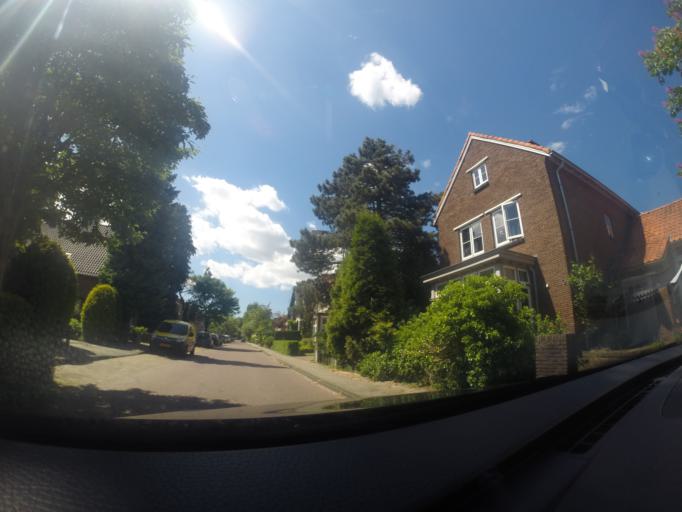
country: NL
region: Gelderland
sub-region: Gemeente Renkum
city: Oosterbeek
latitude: 51.9902
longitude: 5.8368
